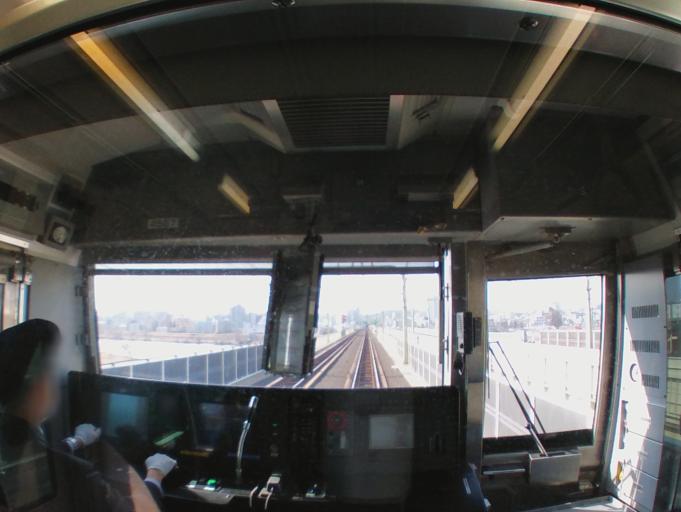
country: JP
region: Tokyo
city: Chofugaoka
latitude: 35.6280
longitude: 139.5740
